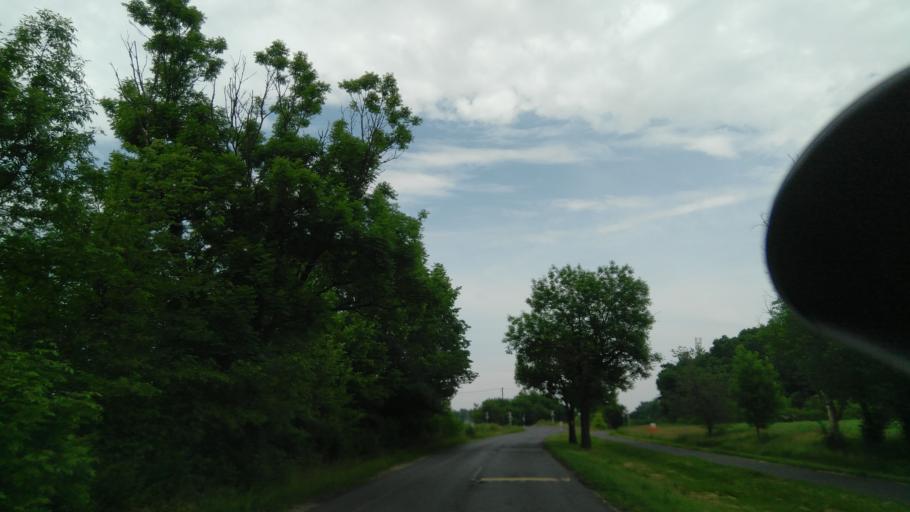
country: HU
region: Bekes
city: Fuzesgyarmat
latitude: 47.0774
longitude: 21.1949
